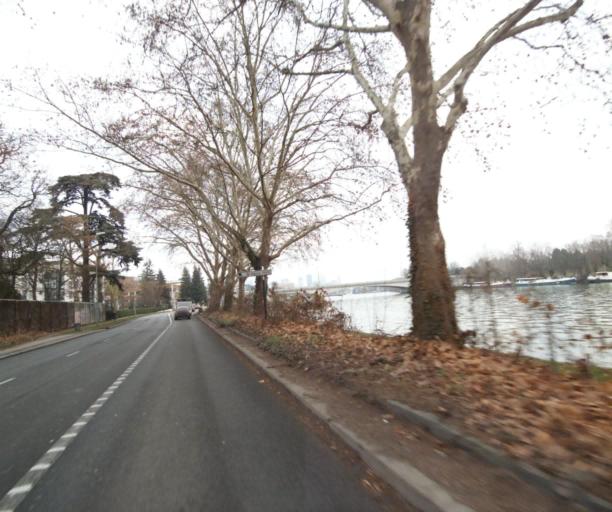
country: FR
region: Ile-de-France
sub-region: Departement des Hauts-de-Seine
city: Suresnes
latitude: 48.8647
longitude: 2.2268
